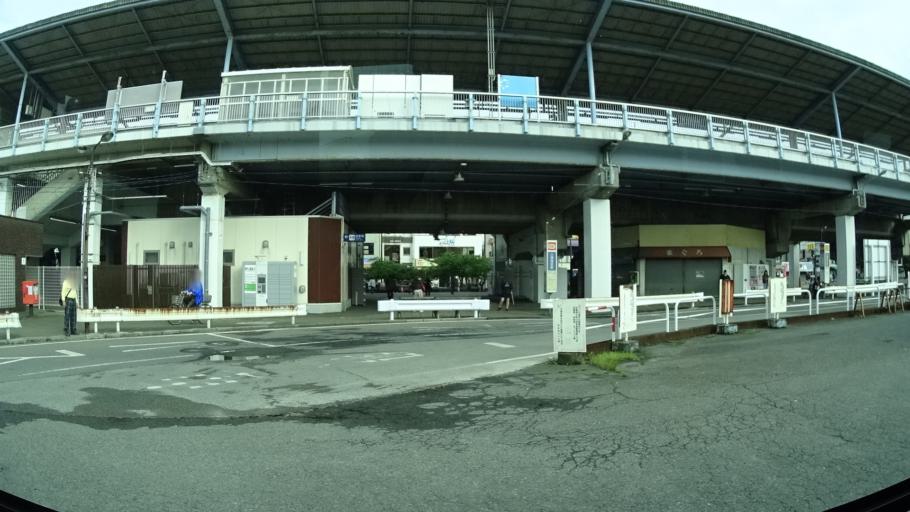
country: JP
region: Kanagawa
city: Miura
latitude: 35.1882
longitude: 139.6529
